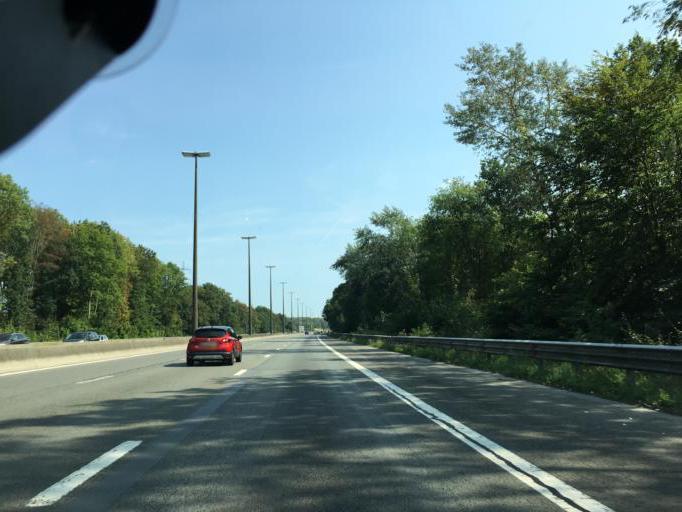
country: BE
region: Wallonia
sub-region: Province du Hainaut
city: Manage
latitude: 50.4947
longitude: 4.2534
